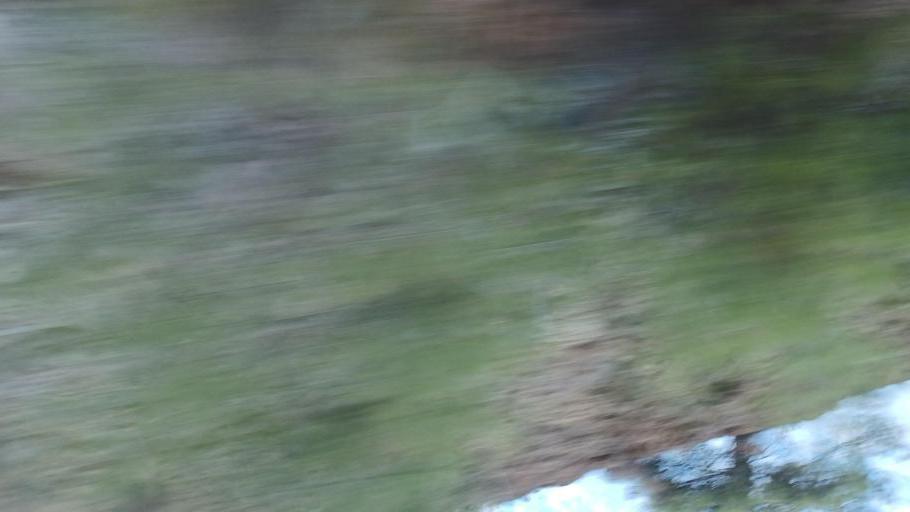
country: CY
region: Limassol
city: Pelendri
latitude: 34.8389
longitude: 32.9549
